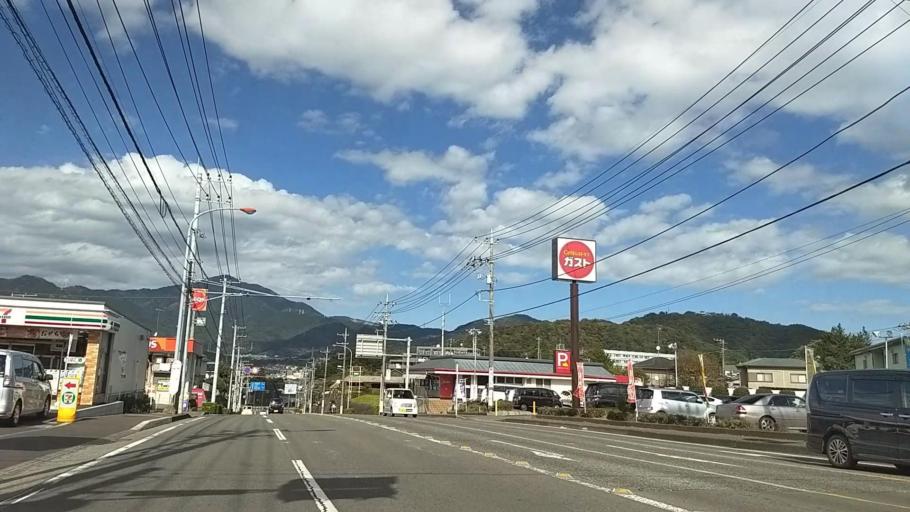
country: JP
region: Kanagawa
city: Hadano
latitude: 35.3614
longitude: 139.2338
